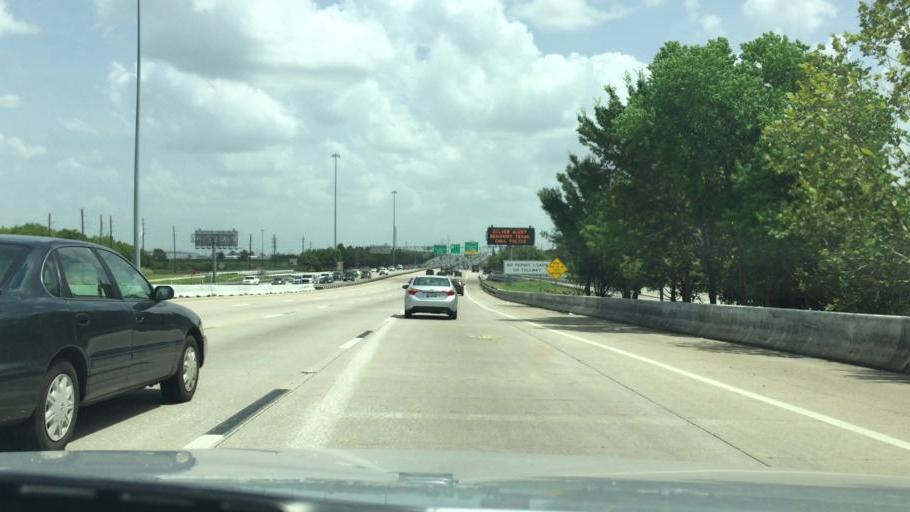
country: US
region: Texas
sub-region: Harris County
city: Hudson
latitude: 29.9520
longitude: -95.5362
